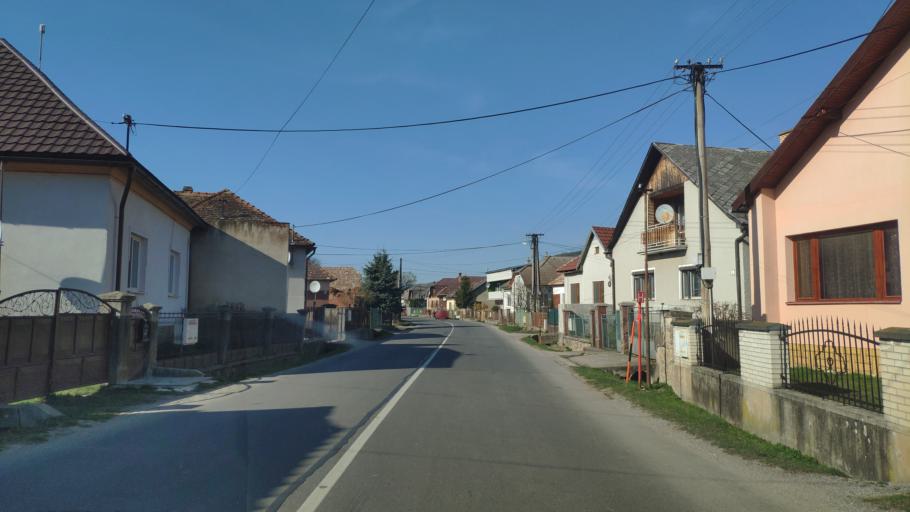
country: SK
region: Banskobystricky
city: Revuca
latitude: 48.5401
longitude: 20.2978
